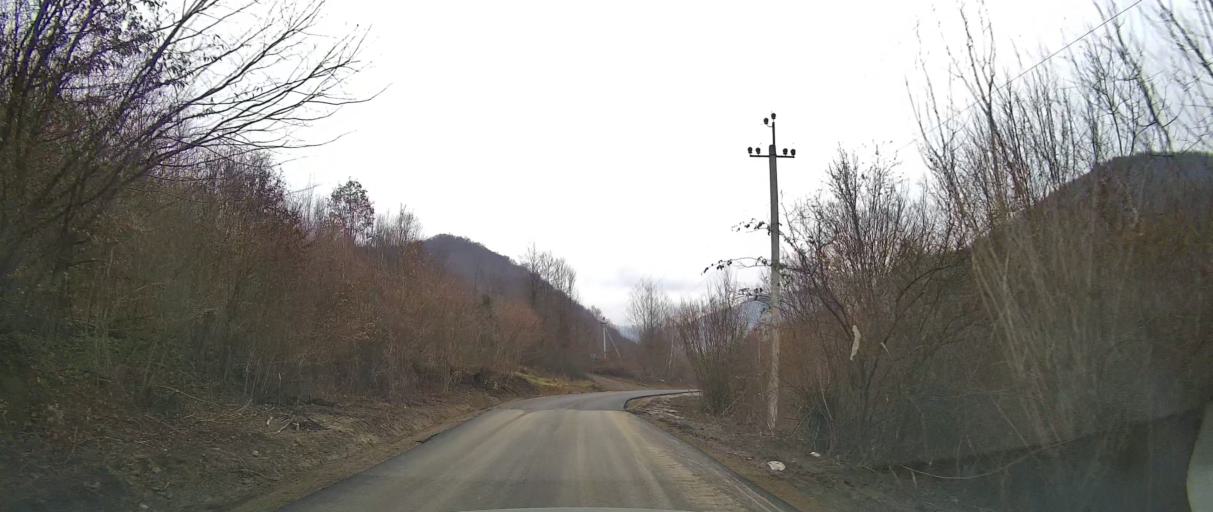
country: UA
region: Zakarpattia
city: Velykyi Bereznyi
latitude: 48.9553
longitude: 22.5461
